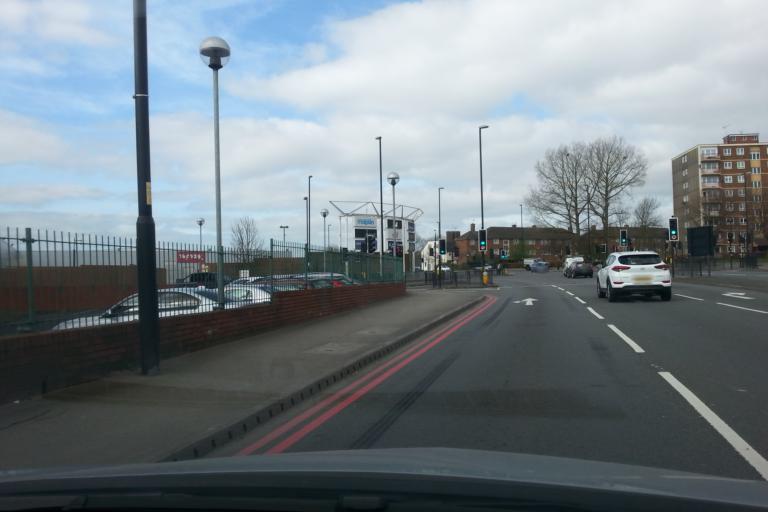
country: GB
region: England
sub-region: Walsall
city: Walsall
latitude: 52.5883
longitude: -1.9863
